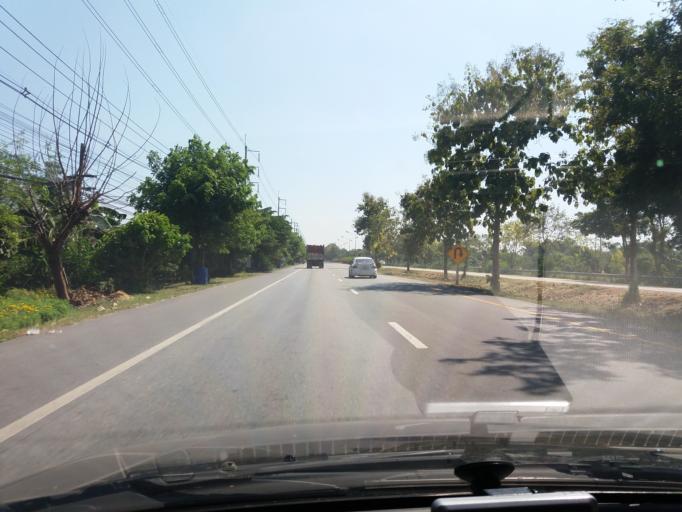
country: TH
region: Chai Nat
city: Sankhaburi
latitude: 15.0877
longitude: 100.1396
